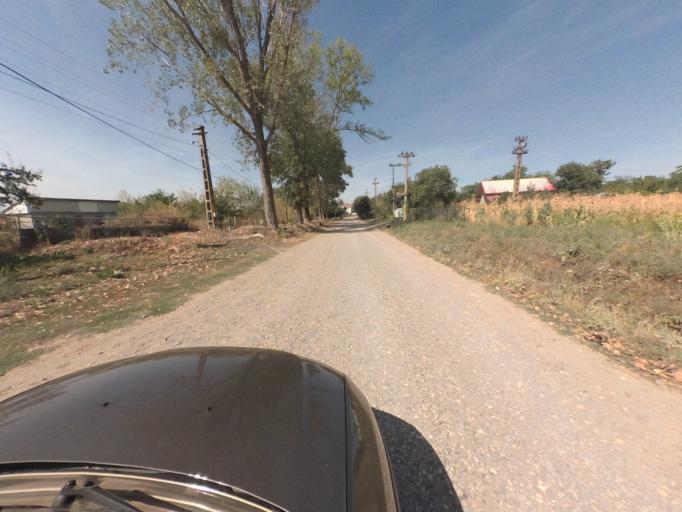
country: RO
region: Vaslui
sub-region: Comuna Deleni
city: Deleni
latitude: 46.5403
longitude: 27.7479
